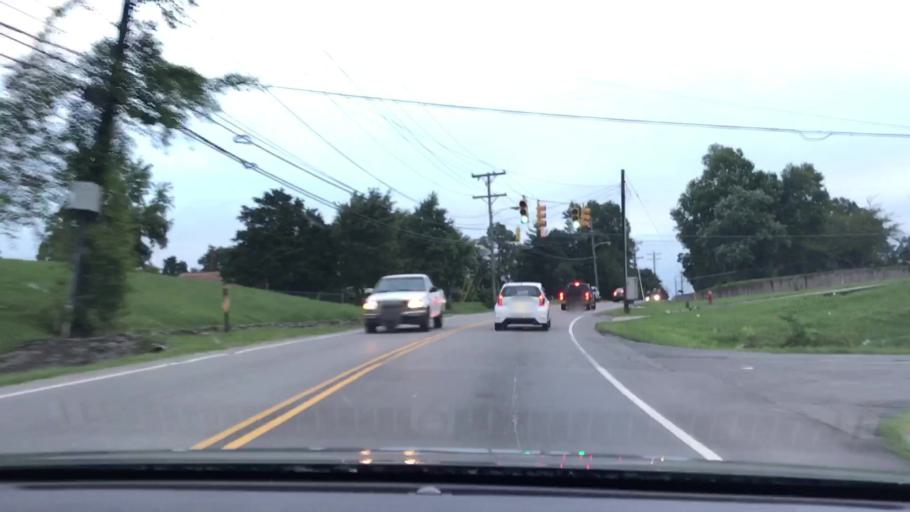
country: US
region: Tennessee
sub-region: Davidson County
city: Oak Hill
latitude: 36.0688
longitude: -86.7175
